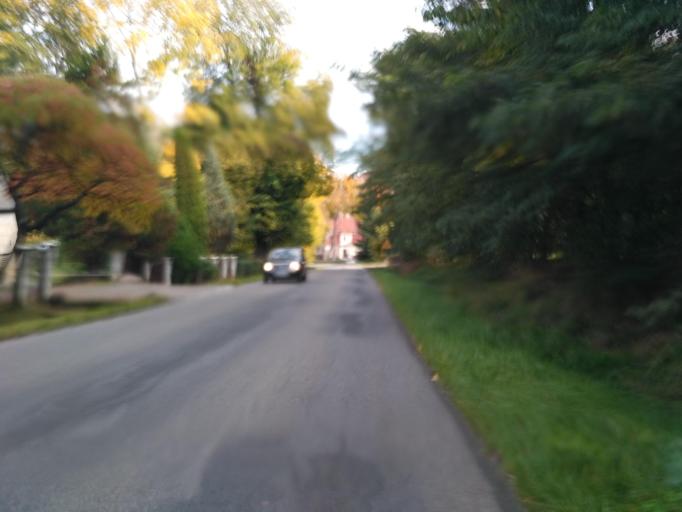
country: PL
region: Subcarpathian Voivodeship
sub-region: Powiat debicki
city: Brzostek
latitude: 49.8862
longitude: 21.3614
